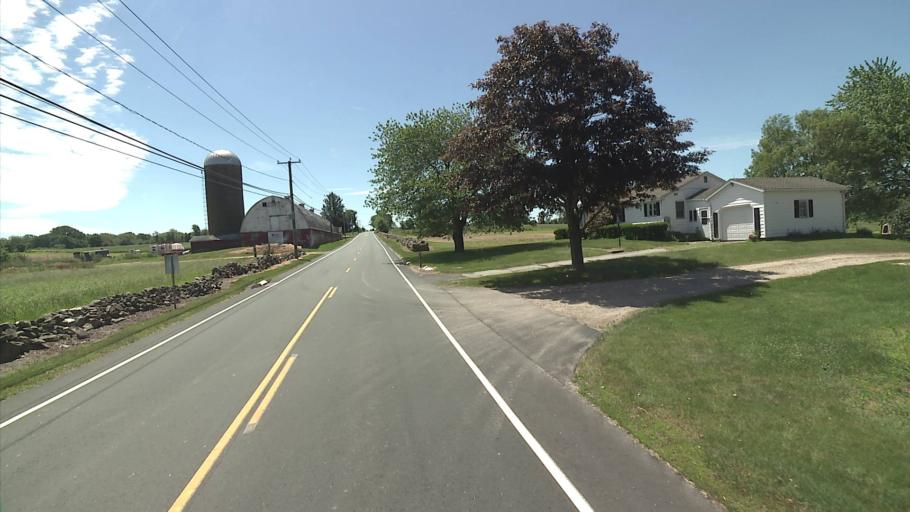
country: US
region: Connecticut
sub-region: Windham County
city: Moosup
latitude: 41.6739
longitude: -71.8507
